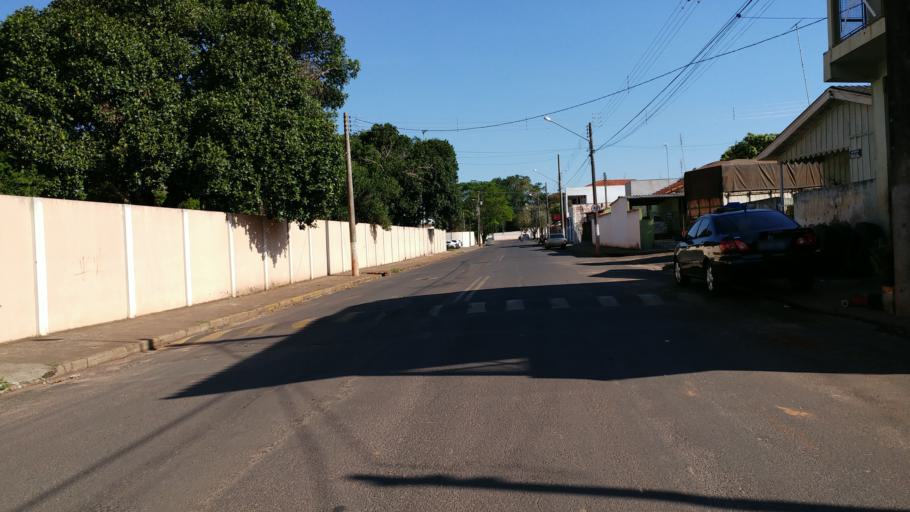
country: BR
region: Sao Paulo
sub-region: Paraguacu Paulista
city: Paraguacu Paulista
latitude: -22.4255
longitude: -50.5764
